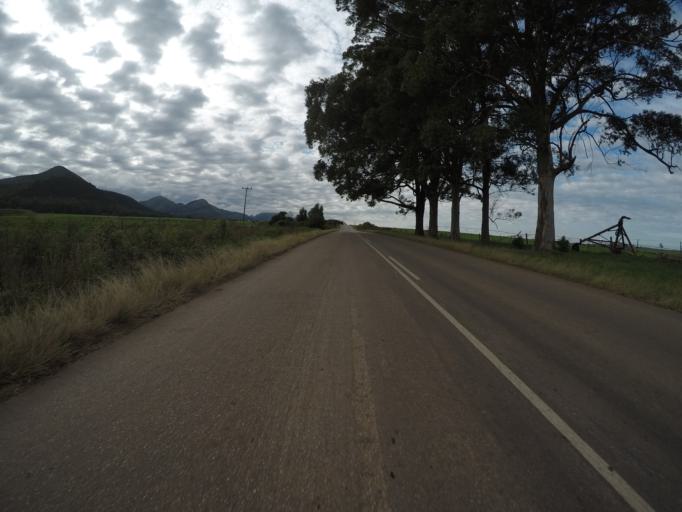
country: ZA
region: Eastern Cape
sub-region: Cacadu District Municipality
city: Kareedouw
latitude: -34.0101
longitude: 24.2768
